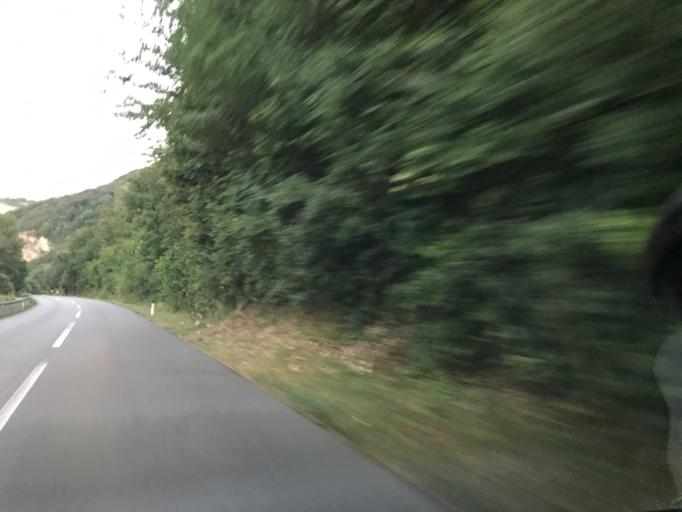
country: RO
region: Caras-Severin
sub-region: Comuna Pescari
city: Coronini
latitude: 44.6527
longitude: 21.7152
